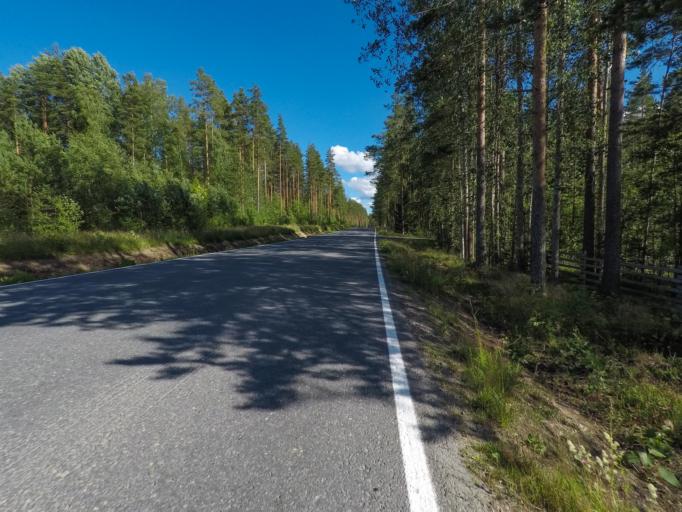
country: FI
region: South Karelia
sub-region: Lappeenranta
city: Taipalsaari
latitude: 61.1782
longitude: 28.0093
